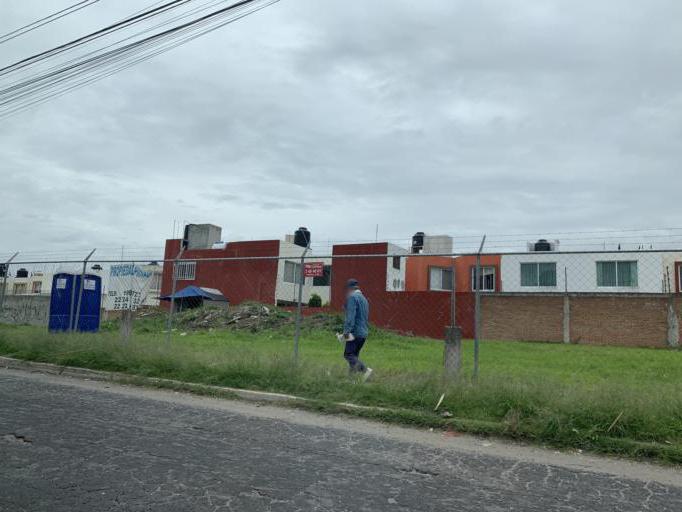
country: MX
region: Puebla
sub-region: Puebla
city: Galaxia la Calera
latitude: 19.0002
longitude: -98.1938
